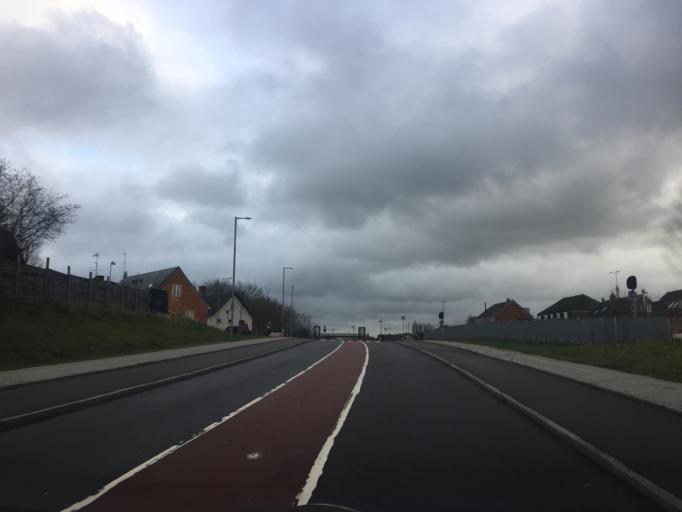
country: DK
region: Zealand
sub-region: Holbaek Kommune
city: Tollose
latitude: 55.6137
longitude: 11.7711
